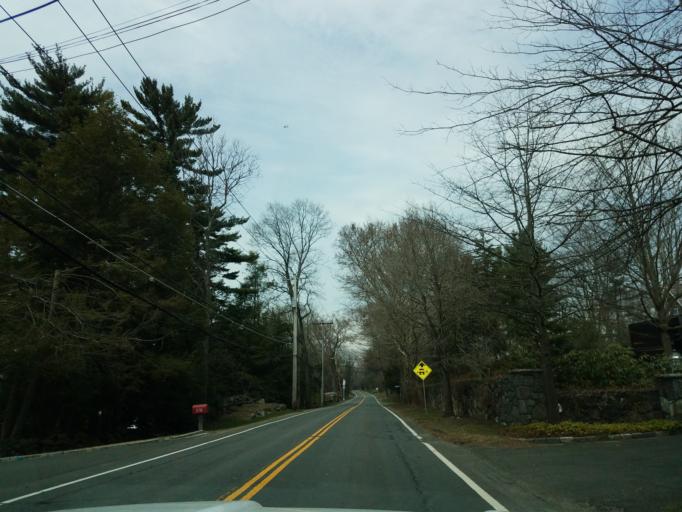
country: US
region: Connecticut
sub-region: Fairfield County
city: Greenwich
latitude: 41.0384
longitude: -73.6341
